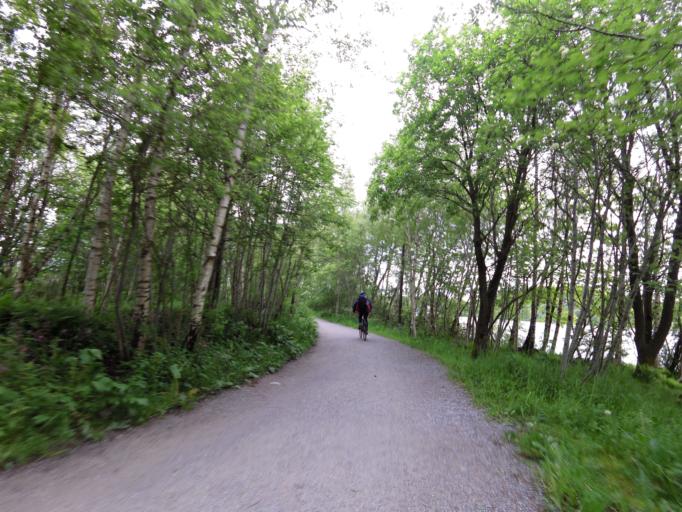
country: NO
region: Rogaland
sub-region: Stavanger
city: Stavanger
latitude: 58.9570
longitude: 5.6751
